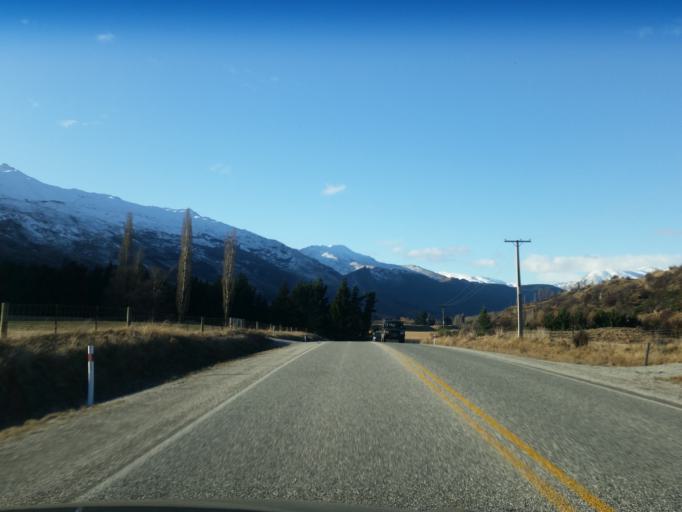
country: NZ
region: Otago
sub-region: Queenstown-Lakes District
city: Queenstown
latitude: -44.9686
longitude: 168.7047
